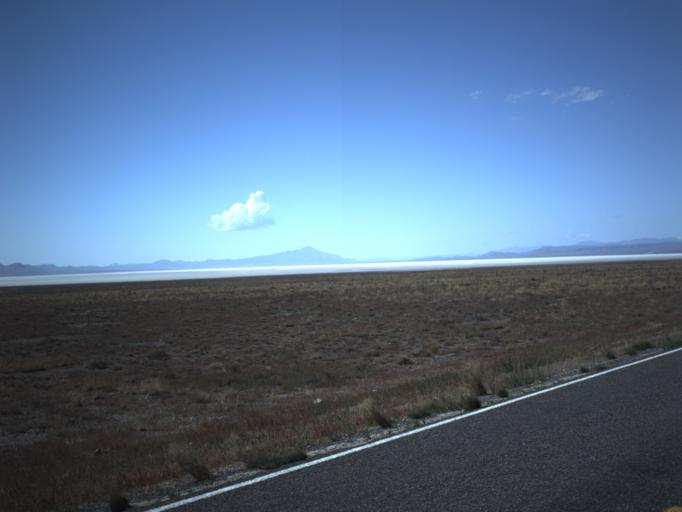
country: US
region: Utah
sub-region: Millard County
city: Delta
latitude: 39.1390
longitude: -113.0885
